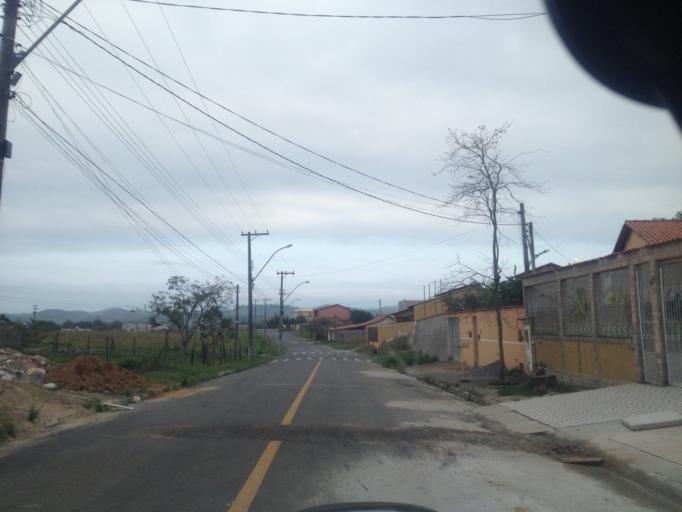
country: BR
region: Rio de Janeiro
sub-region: Porto Real
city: Porto Real
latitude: -22.4099
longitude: -44.3112
